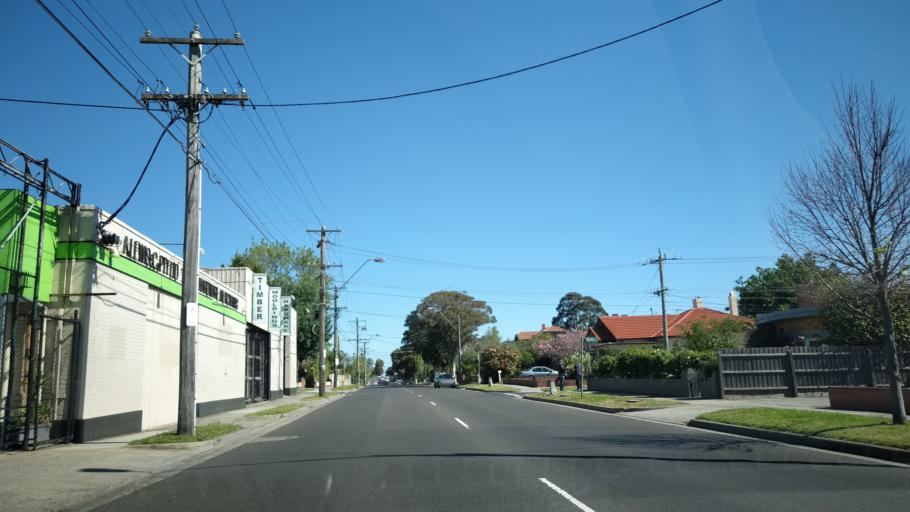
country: AU
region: Victoria
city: McKinnon
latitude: -37.9079
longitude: 145.0435
